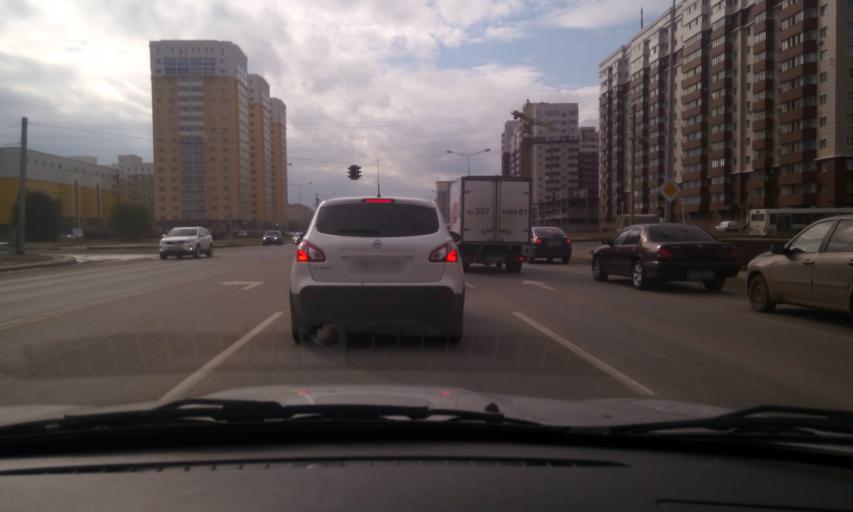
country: KZ
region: Astana Qalasy
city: Astana
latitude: 51.1317
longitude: 71.5065
